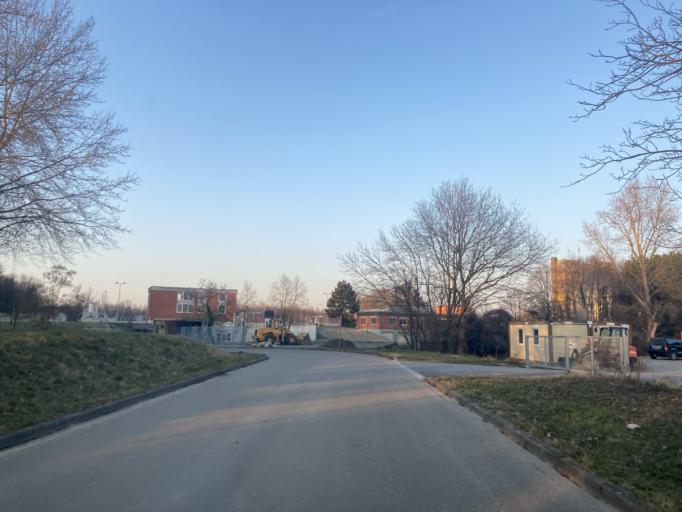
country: DE
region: Baden-Wuerttemberg
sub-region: Freiburg Region
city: Breisach am Rhein
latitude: 48.0478
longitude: 7.5786
